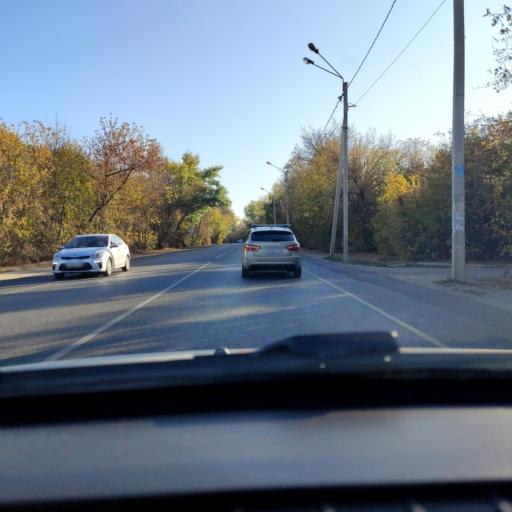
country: RU
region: Voronezj
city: Voronezh
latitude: 51.6023
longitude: 39.1777
